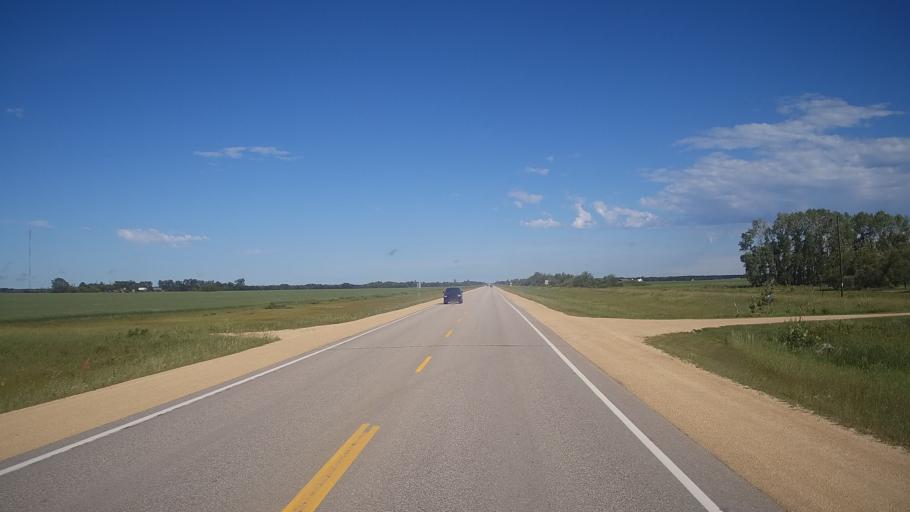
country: CA
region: Manitoba
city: Stonewall
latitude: 50.1836
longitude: -97.6260
